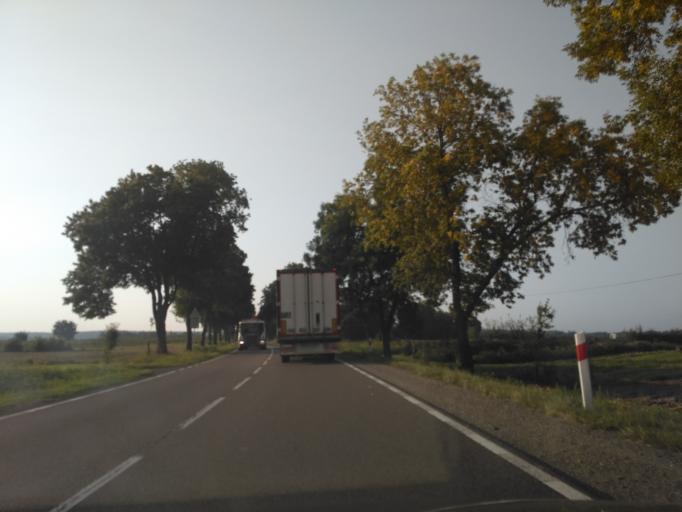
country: PL
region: Lublin Voivodeship
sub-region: Powiat krasnicki
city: Krasnik
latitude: 50.8815
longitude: 22.2615
